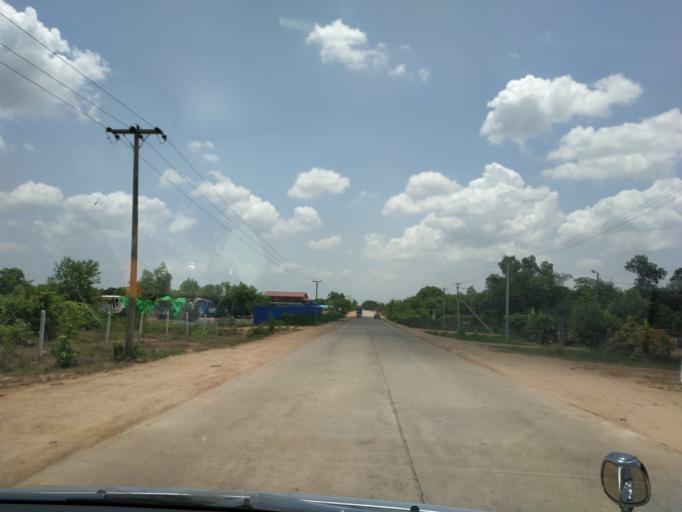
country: MM
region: Bago
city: Bago
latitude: 17.4753
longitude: 96.4766
